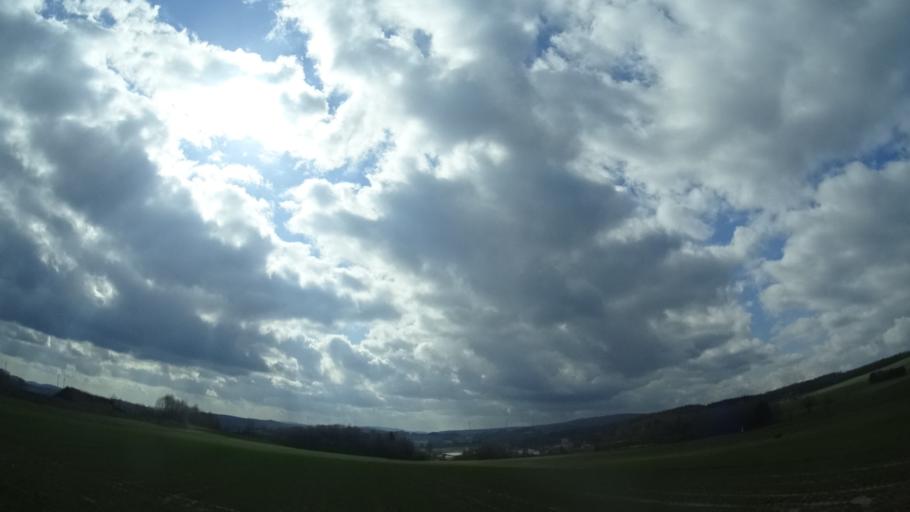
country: DE
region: Rheinland-Pfalz
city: Gollenberg
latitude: 49.6679
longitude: 7.1608
